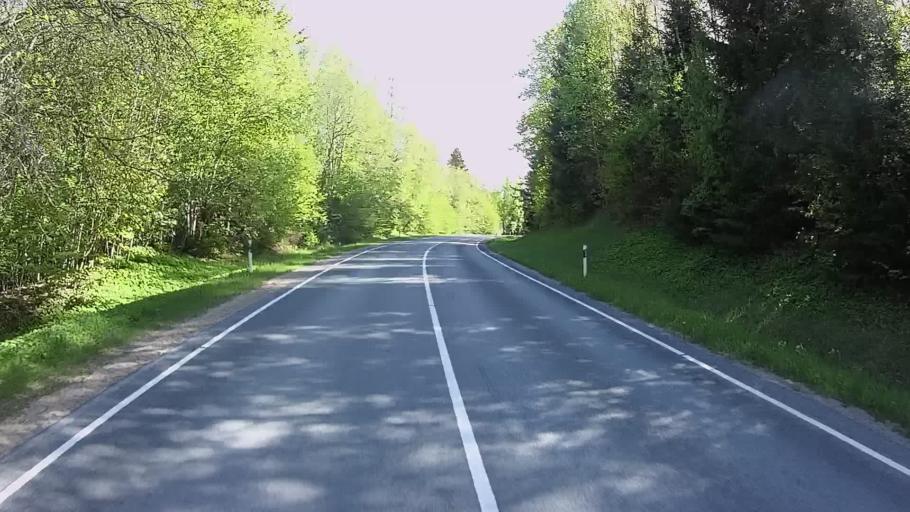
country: EE
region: Vorumaa
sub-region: Antsla vald
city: Vana-Antsla
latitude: 57.9686
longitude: 26.4623
